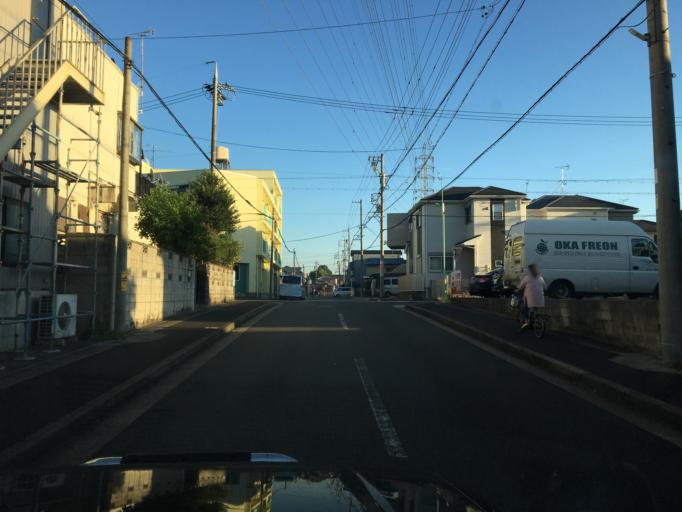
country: JP
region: Aichi
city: Kasugai
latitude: 35.1966
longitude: 137.0028
